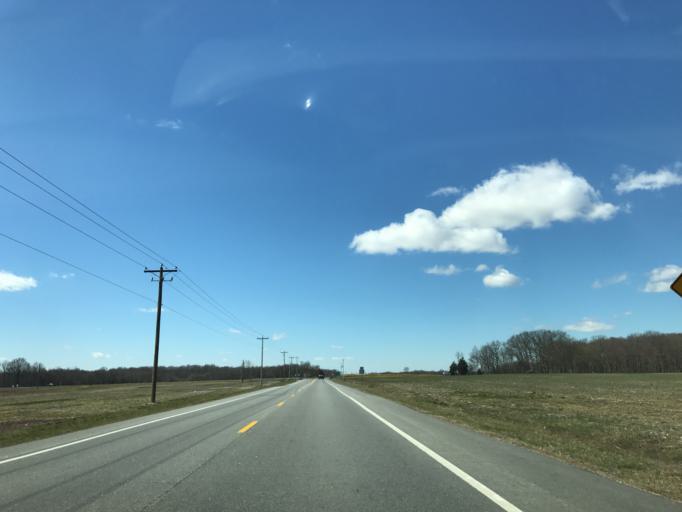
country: US
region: Maryland
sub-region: Queen Anne's County
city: Kingstown
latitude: 39.1221
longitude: -75.9388
